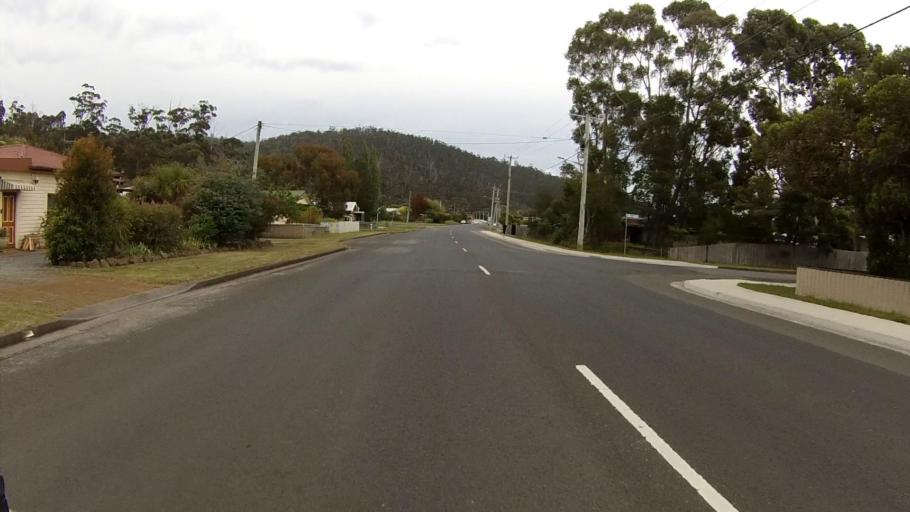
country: AU
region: Tasmania
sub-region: Sorell
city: Sorell
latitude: -42.5616
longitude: 147.8724
